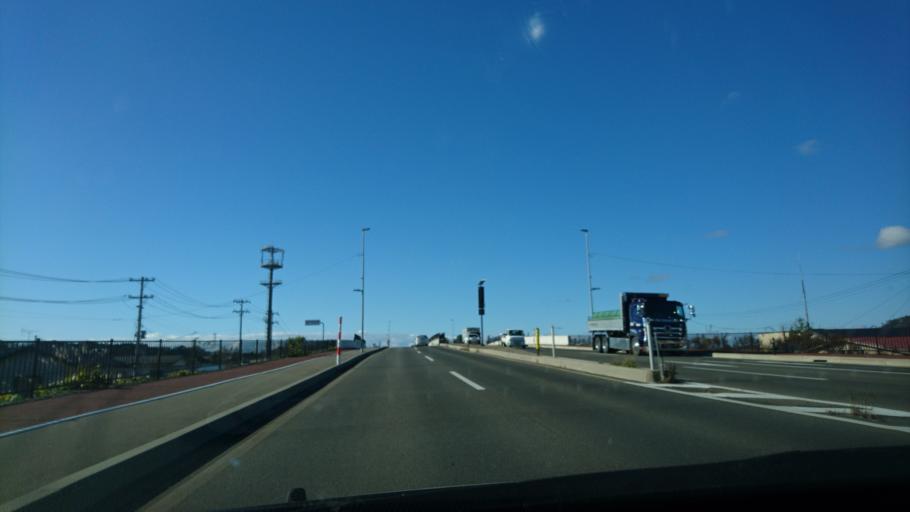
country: JP
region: Akita
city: Akita Shi
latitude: 39.3801
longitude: 140.0556
